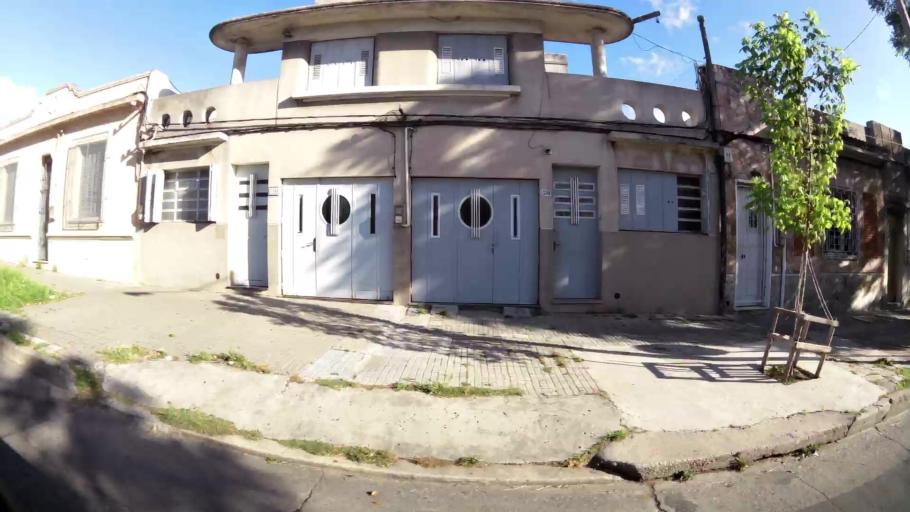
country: UY
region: Montevideo
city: Montevideo
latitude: -34.8785
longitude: -56.1507
